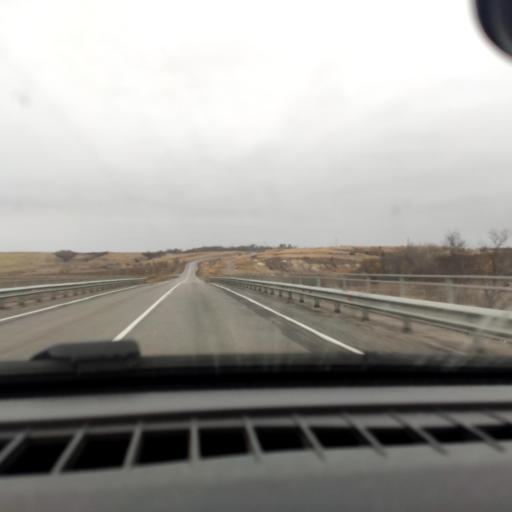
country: RU
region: Voronezj
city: Uryv-Pokrovka
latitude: 51.1302
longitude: 39.0435
